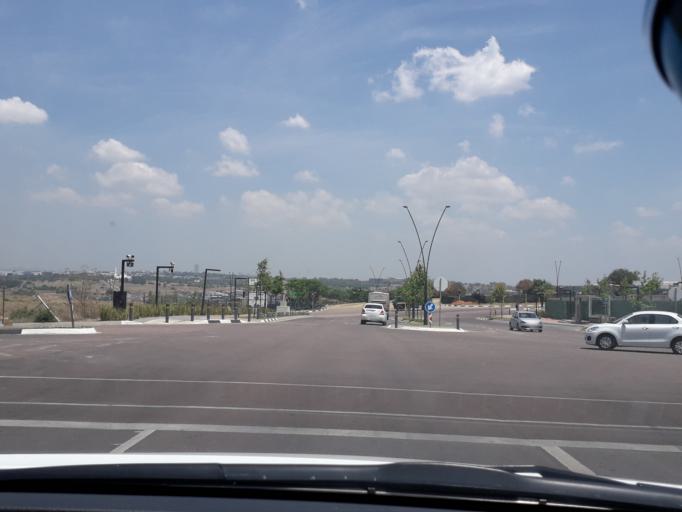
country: ZA
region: Gauteng
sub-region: City of Johannesburg Metropolitan Municipality
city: Midrand
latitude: -26.0176
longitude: 28.1083
